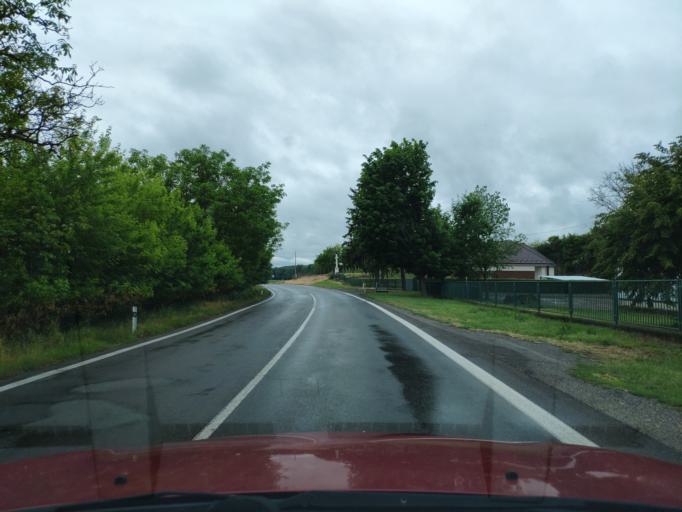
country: HU
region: Borsod-Abauj-Zemplen
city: Karcsa
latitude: 48.3915
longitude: 21.7710
